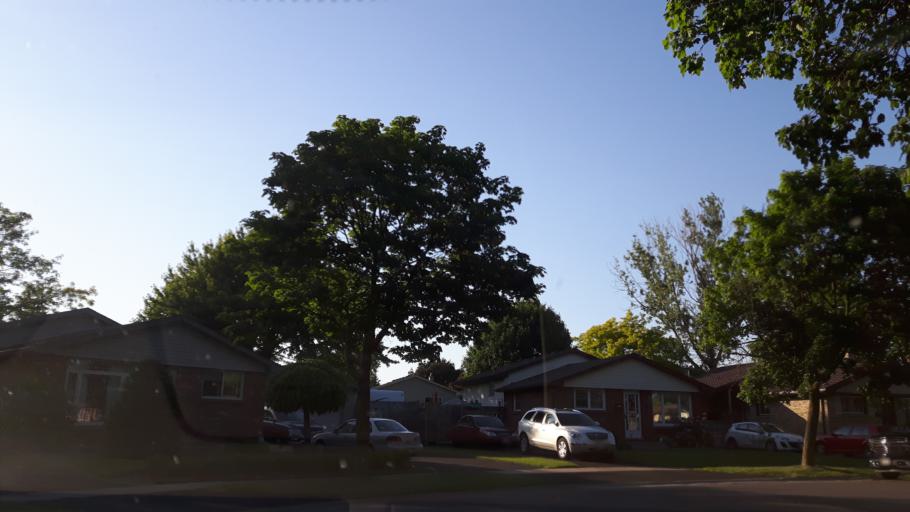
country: CA
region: Ontario
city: London
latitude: 42.9399
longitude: -81.2098
